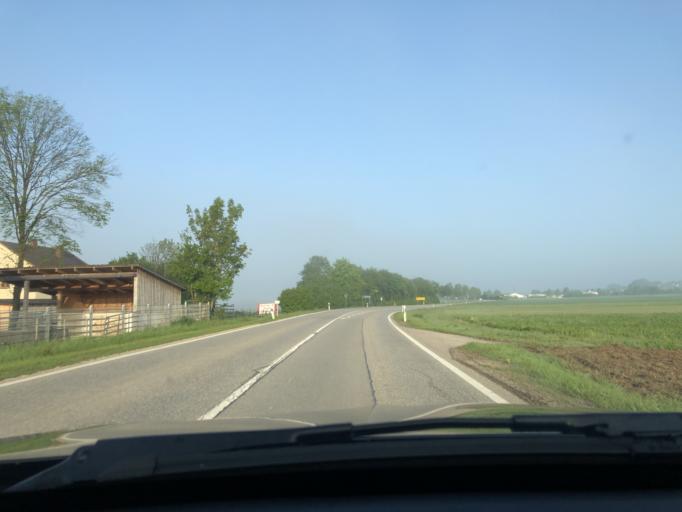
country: DE
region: Bavaria
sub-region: Upper Bavaria
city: Kirchdorf
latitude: 48.4578
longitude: 11.6721
